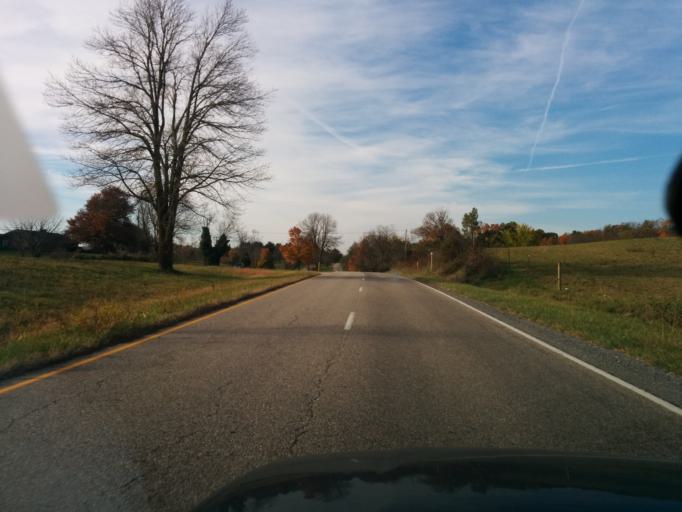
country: US
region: Virginia
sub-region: Rockbridge County
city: East Lexington
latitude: 37.8650
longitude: -79.3144
